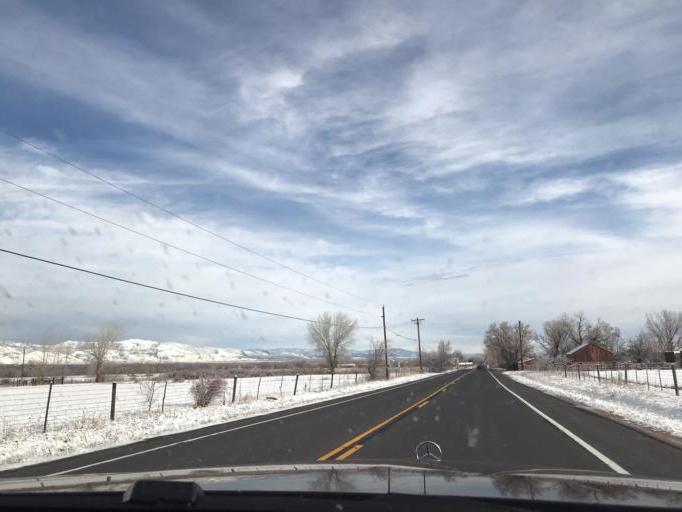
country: US
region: Colorado
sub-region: Boulder County
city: Superior
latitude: 39.9791
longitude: -105.2128
